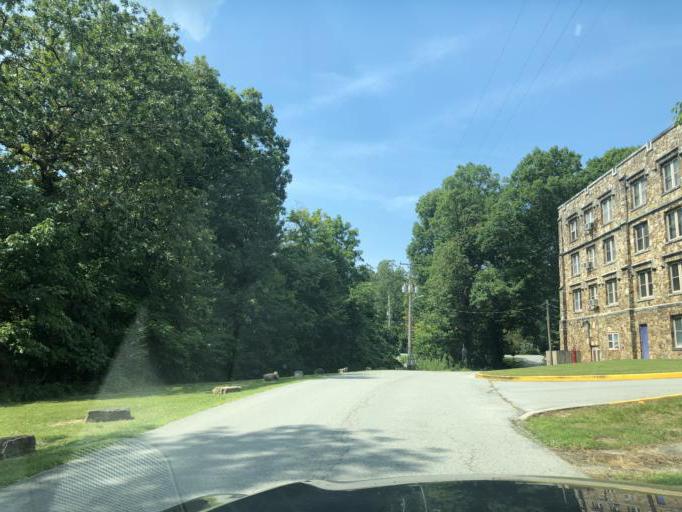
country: US
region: Tennessee
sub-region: Franklin County
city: Sewanee
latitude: 35.1966
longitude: -85.9261
